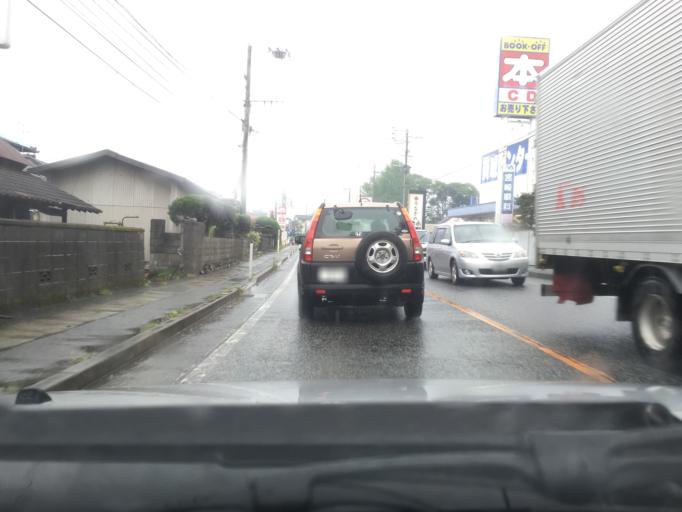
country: JP
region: Kumamoto
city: Ueki
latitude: 32.8731
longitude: 130.7015
